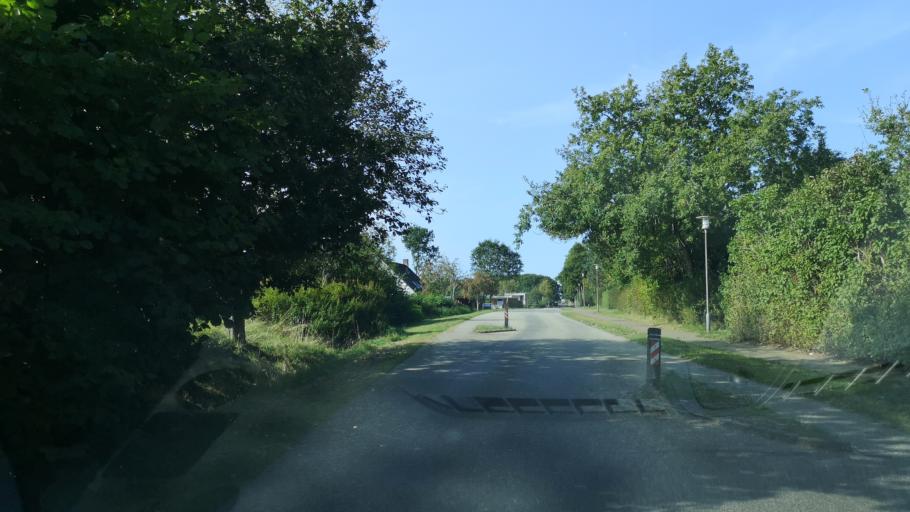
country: DK
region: Central Jutland
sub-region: Herning Kommune
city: Herning
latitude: 56.1672
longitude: 8.9785
